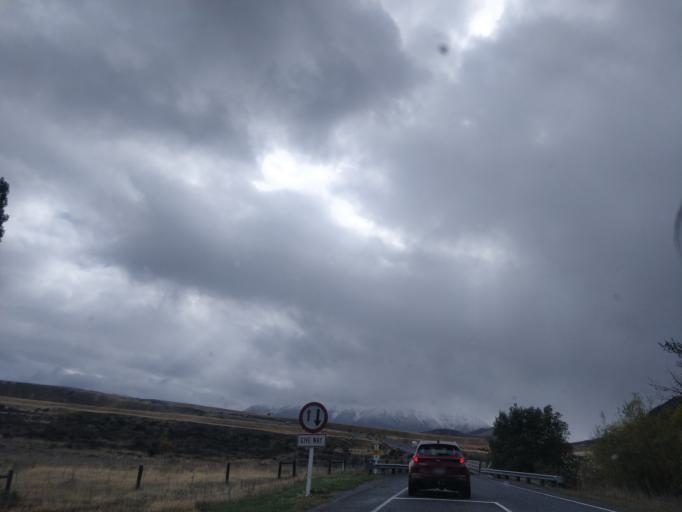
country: NZ
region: Canterbury
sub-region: Ashburton District
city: Methven
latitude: -43.2458
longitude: 171.7250
